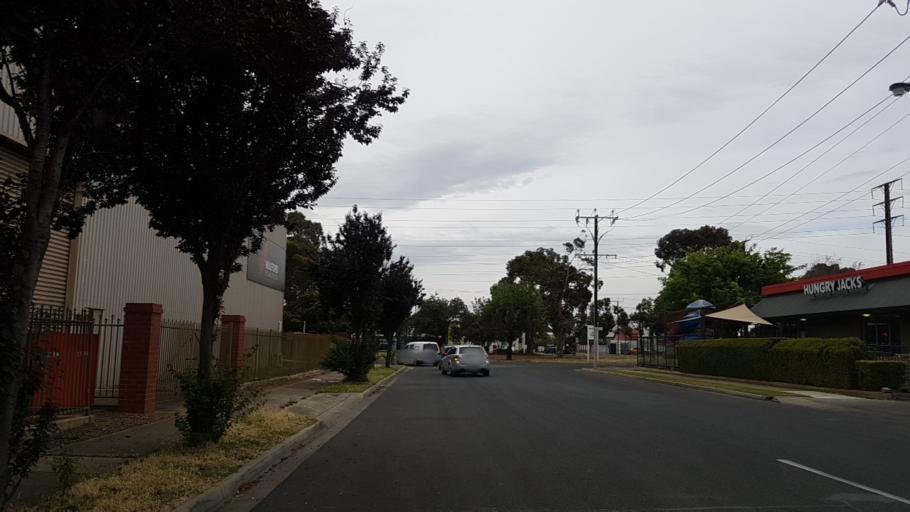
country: AU
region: South Australia
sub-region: Charles Sturt
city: Woodville
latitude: -34.8865
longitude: 138.5422
